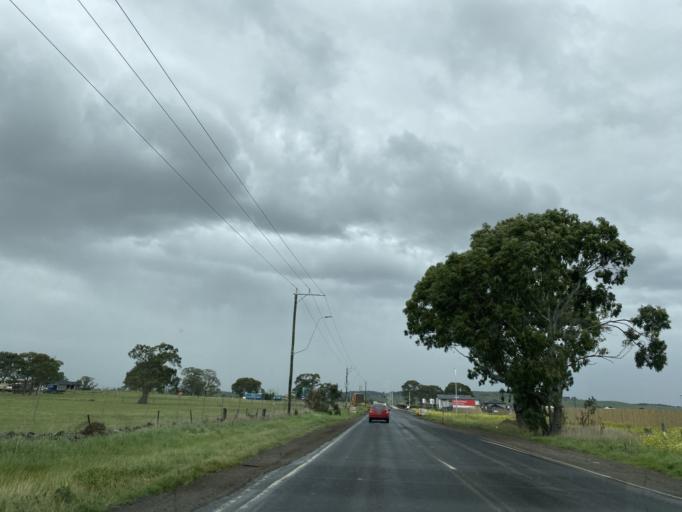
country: AU
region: Victoria
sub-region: Whittlesea
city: Epping
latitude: -37.6074
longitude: 145.0204
